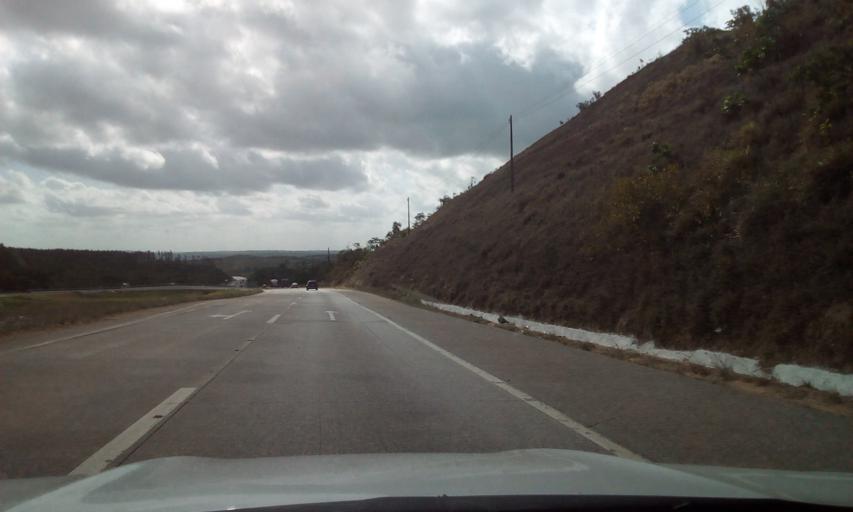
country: BR
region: Sergipe
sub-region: Sao Cristovao
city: Sao Cristovao
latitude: -10.9647
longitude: -37.2661
